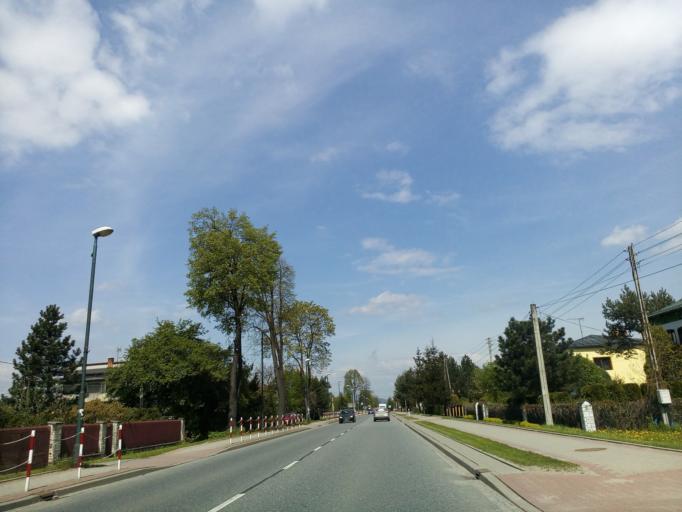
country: PL
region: Lesser Poland Voivodeship
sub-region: Powiat nowosadecki
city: Nawojowa
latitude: 49.5680
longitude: 20.7385
